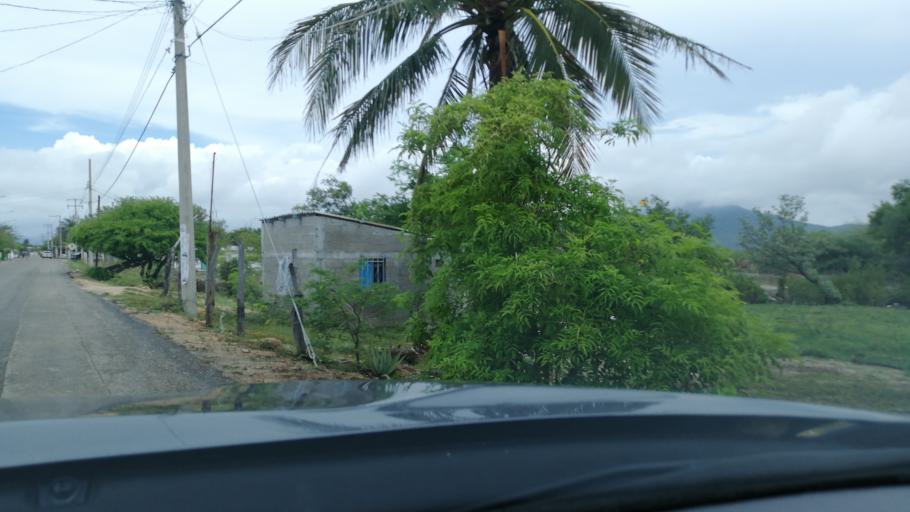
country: MX
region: Oaxaca
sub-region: Salina Cruz
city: Salina Cruz
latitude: 16.1638
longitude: -95.2180
